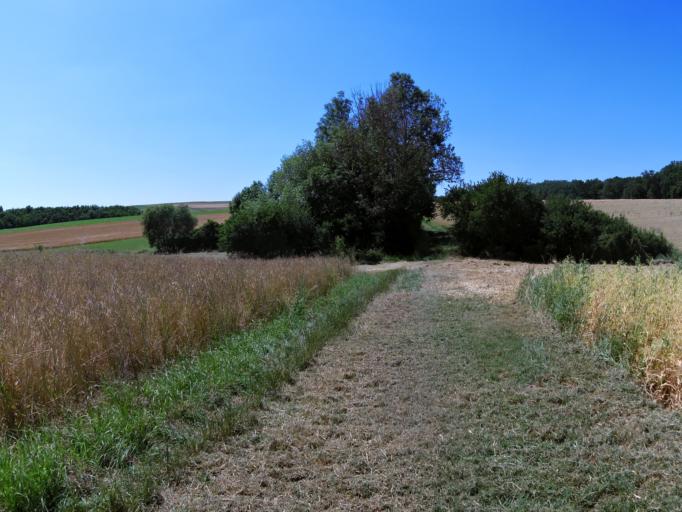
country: DE
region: Bavaria
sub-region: Regierungsbezirk Unterfranken
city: Reichenberg
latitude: 49.7253
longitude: 9.9017
